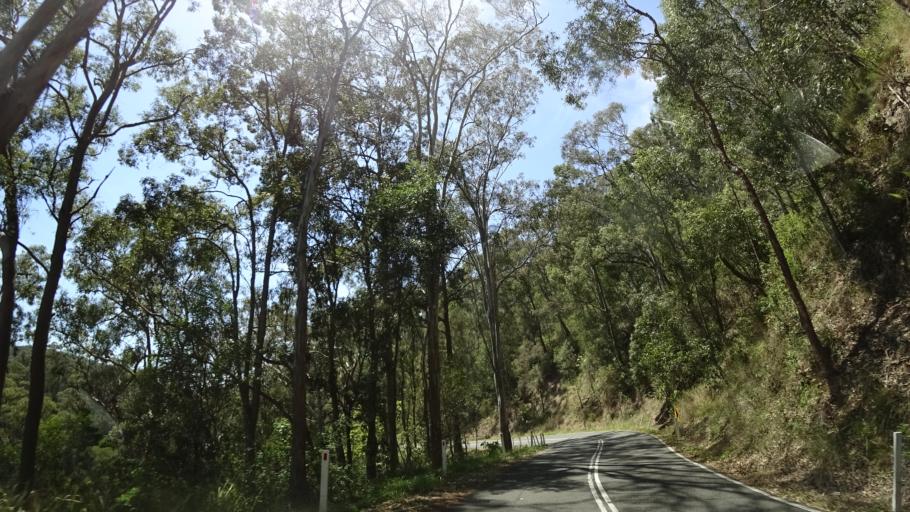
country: AU
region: Queensland
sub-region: Moreton Bay
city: Samford Valley
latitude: -27.4199
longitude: 152.8656
